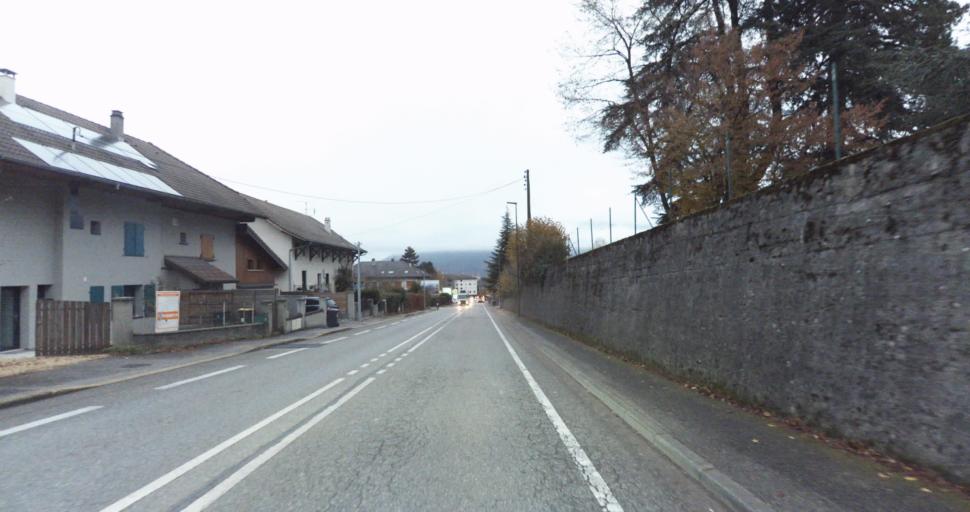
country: FR
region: Rhone-Alpes
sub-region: Departement de la Haute-Savoie
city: Cran-Gevrier
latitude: 45.8937
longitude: 6.1041
